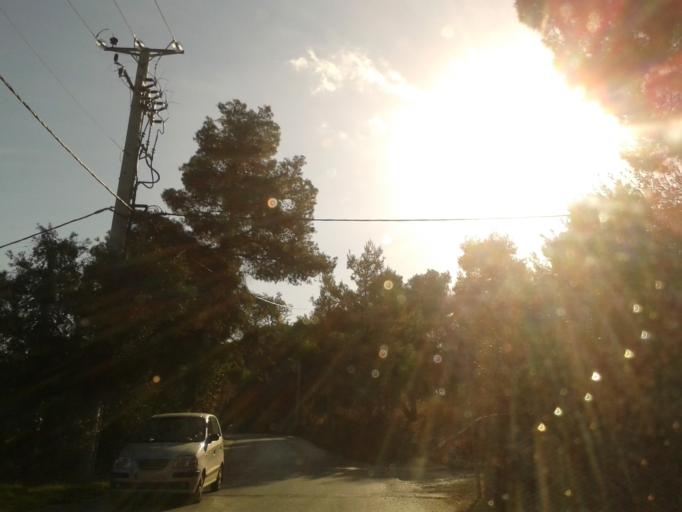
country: GR
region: Attica
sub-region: Nomarchia Anatolikis Attikis
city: Anoixi
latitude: 38.1377
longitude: 23.8673
